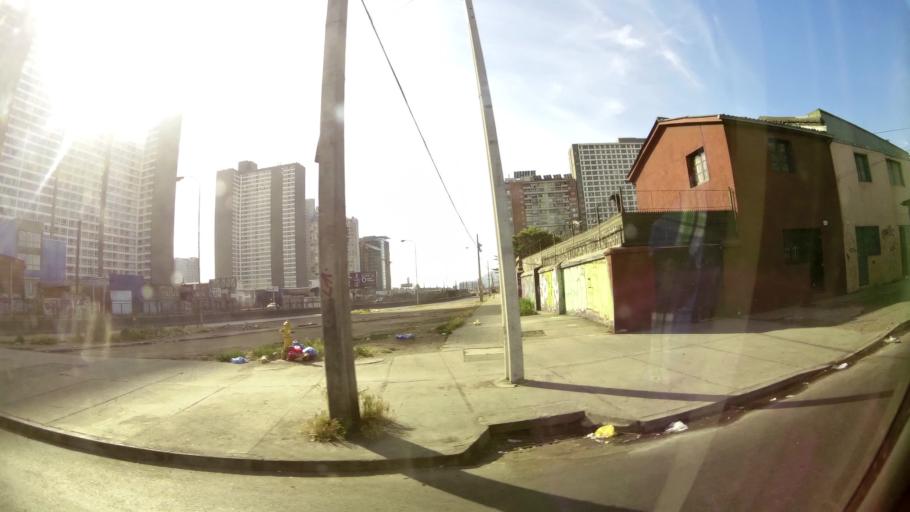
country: CL
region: Santiago Metropolitan
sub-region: Provincia de Santiago
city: Lo Prado
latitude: -33.4577
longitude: -70.6892
